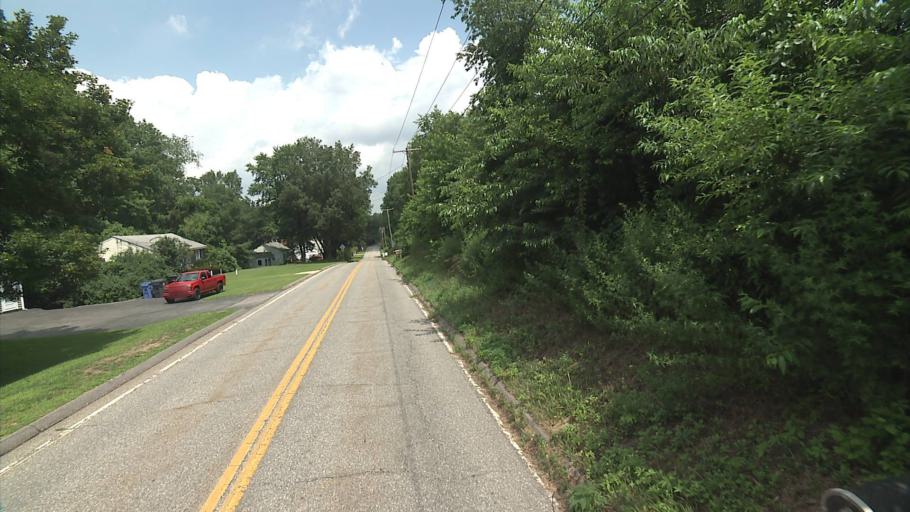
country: US
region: Connecticut
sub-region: New London County
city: Baltic
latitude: 41.6090
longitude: -72.1252
